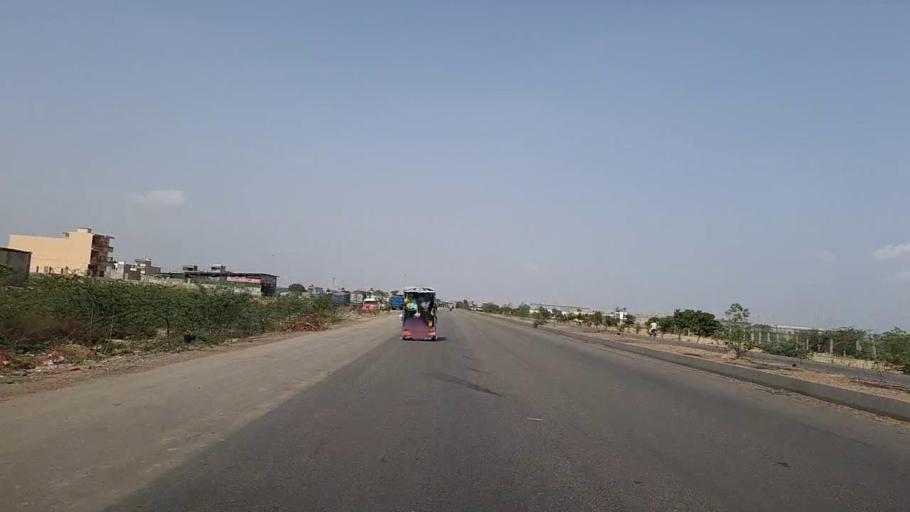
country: PK
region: Sindh
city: Malir Cantonment
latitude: 24.8671
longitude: 67.3693
